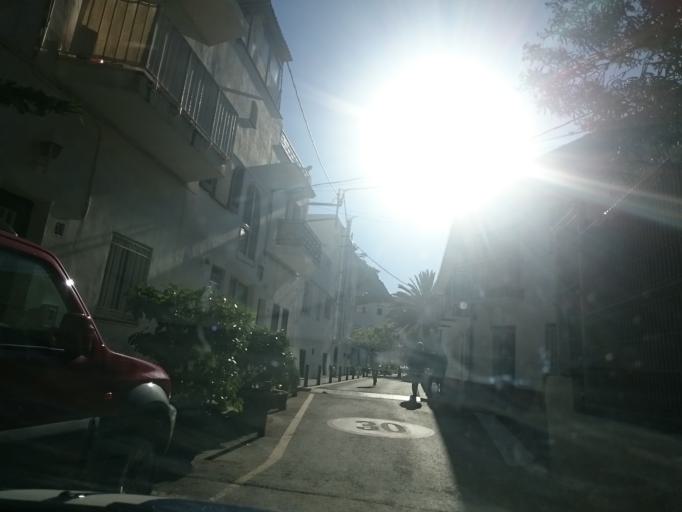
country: ES
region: Catalonia
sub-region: Provincia de Barcelona
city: Castelldefels
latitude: 41.2526
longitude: 1.9006
